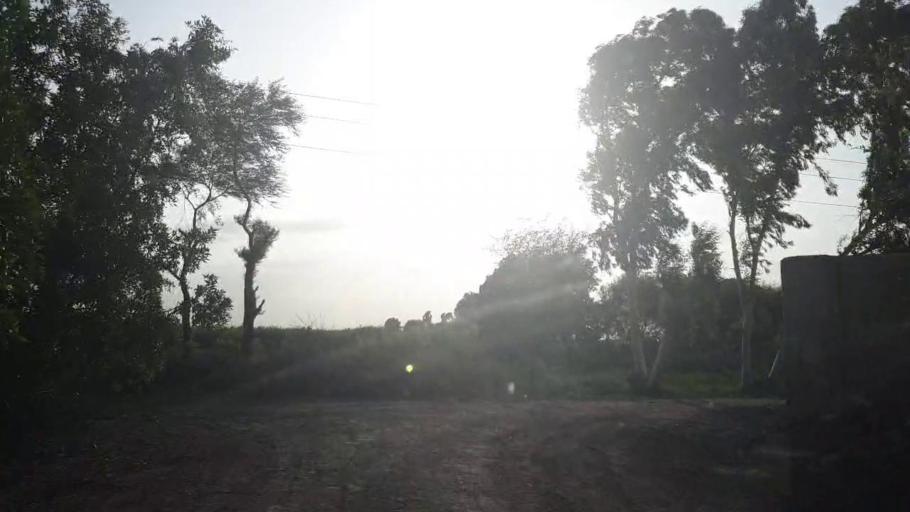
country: PK
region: Sindh
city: Kadhan
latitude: 24.6351
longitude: 69.1563
